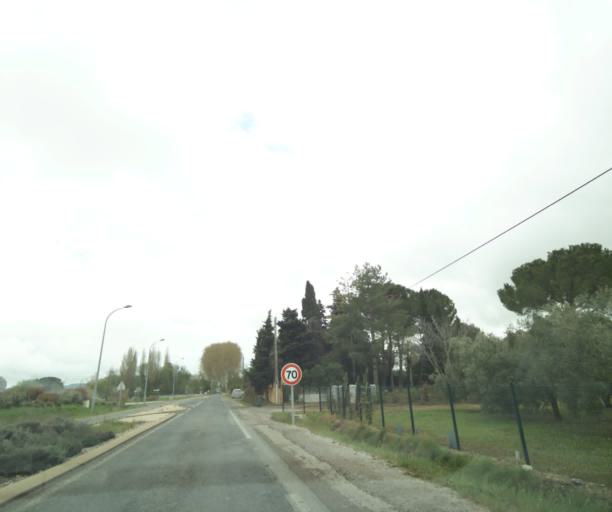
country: FR
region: Languedoc-Roussillon
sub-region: Departement de l'Herault
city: Cournonterral
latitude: 43.5526
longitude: 3.7269
